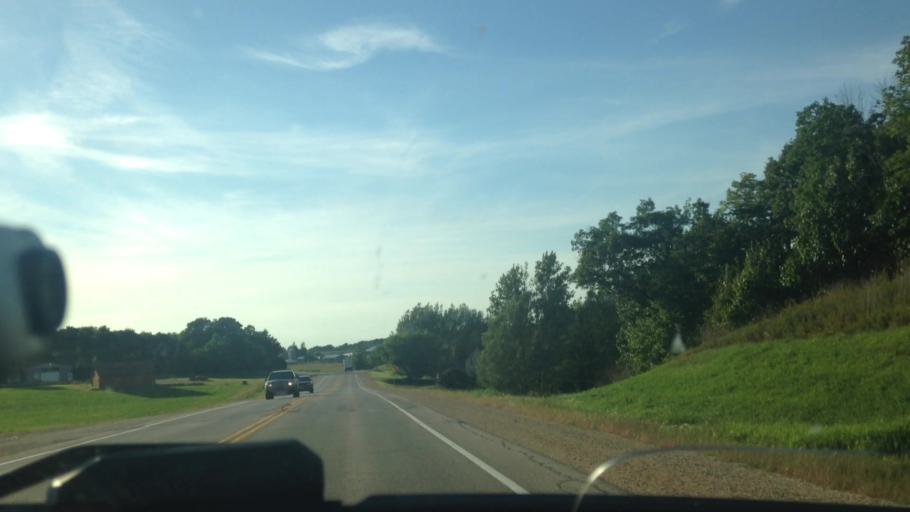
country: US
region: Wisconsin
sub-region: Dodge County
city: Theresa
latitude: 43.4385
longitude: -88.4766
